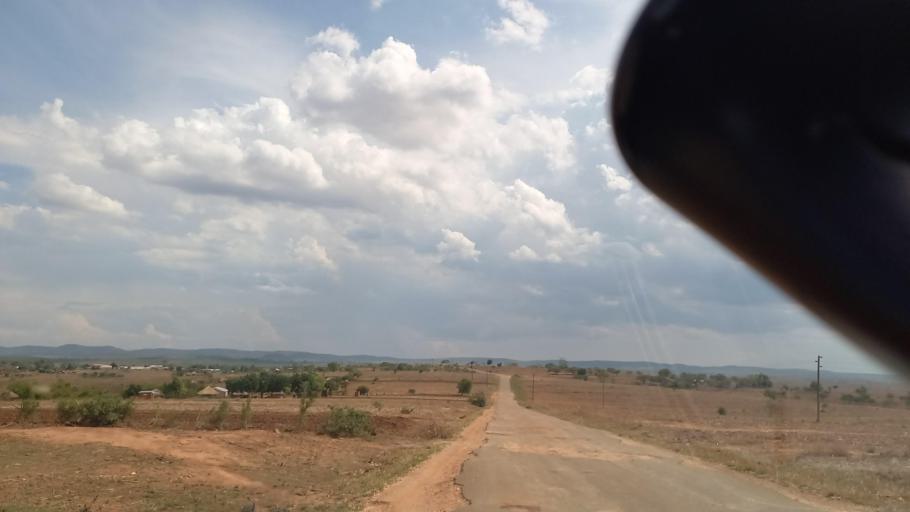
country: ZM
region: Lusaka
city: Kafue
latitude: -16.1793
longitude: 28.0885
